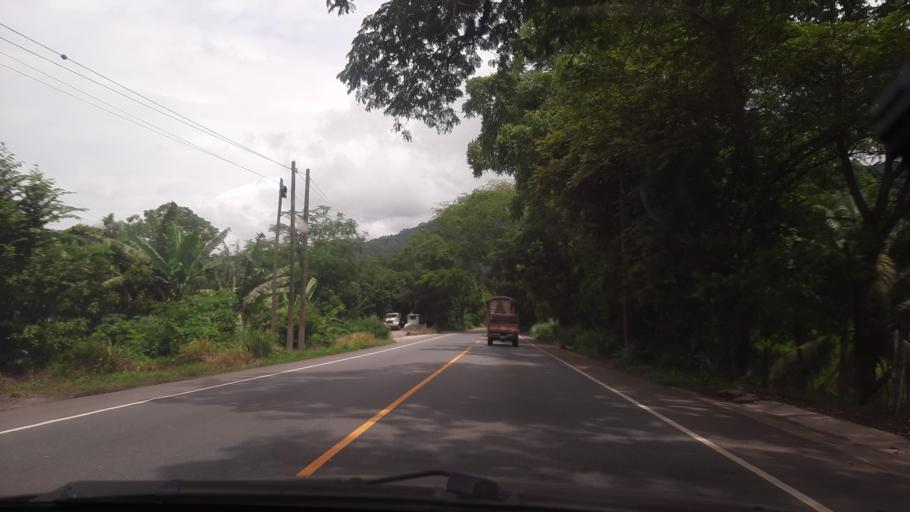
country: GT
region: Zacapa
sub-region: Municipio de Zacapa
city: Gualan
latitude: 15.1971
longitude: -89.2682
